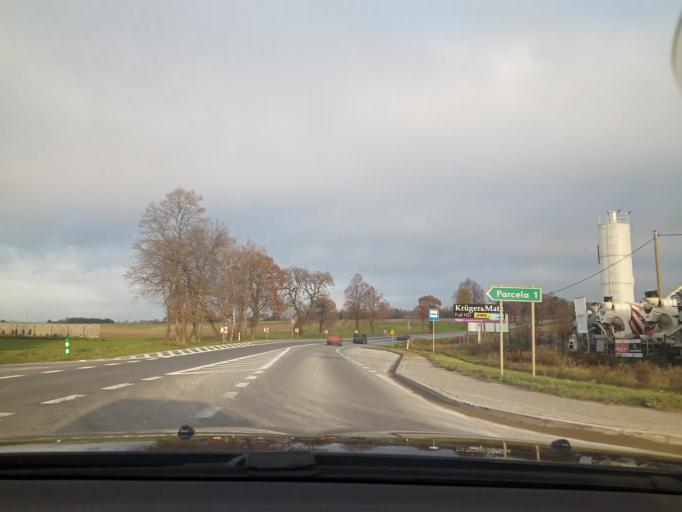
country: PL
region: Lesser Poland Voivodeship
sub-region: Powiat miechowski
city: Miechow
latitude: 50.3235
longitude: 20.0342
